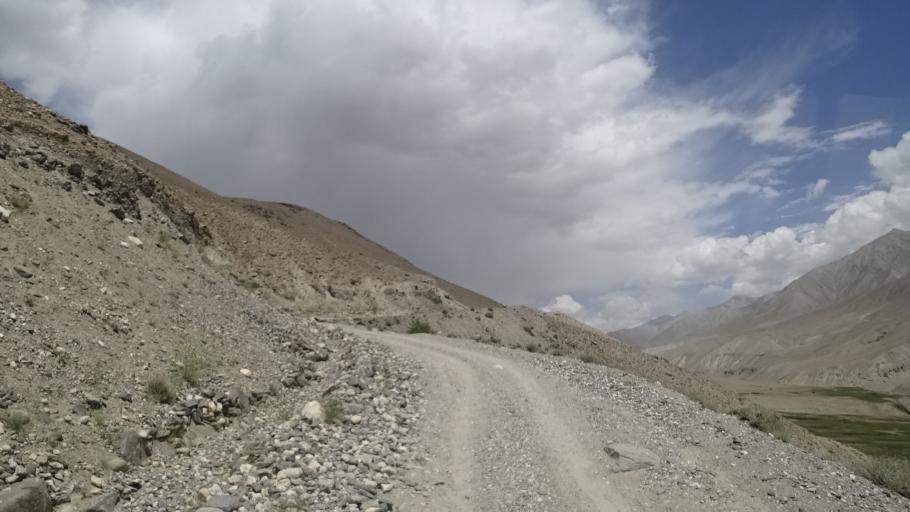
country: AF
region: Badakhshan
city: Khandud
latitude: 37.0848
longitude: 72.7007
